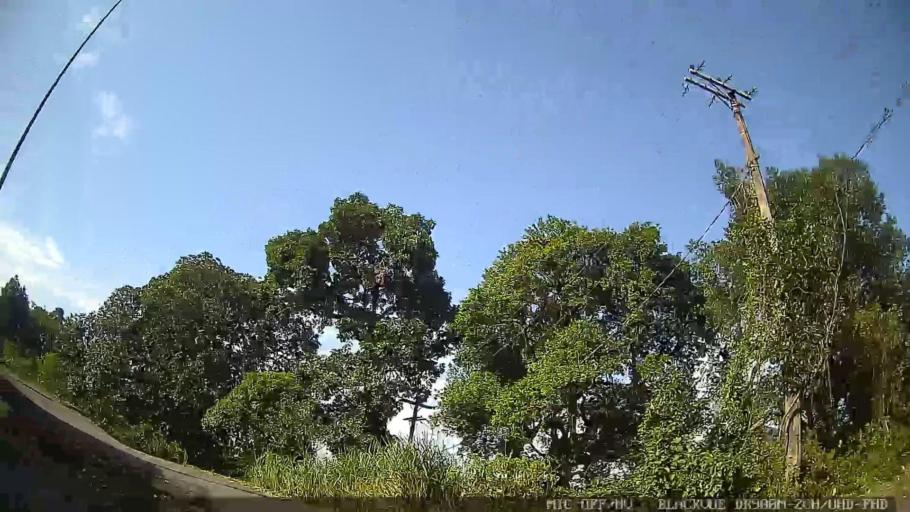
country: BR
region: Sao Paulo
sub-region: Cubatao
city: Cubatao
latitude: -23.8933
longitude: -46.4724
